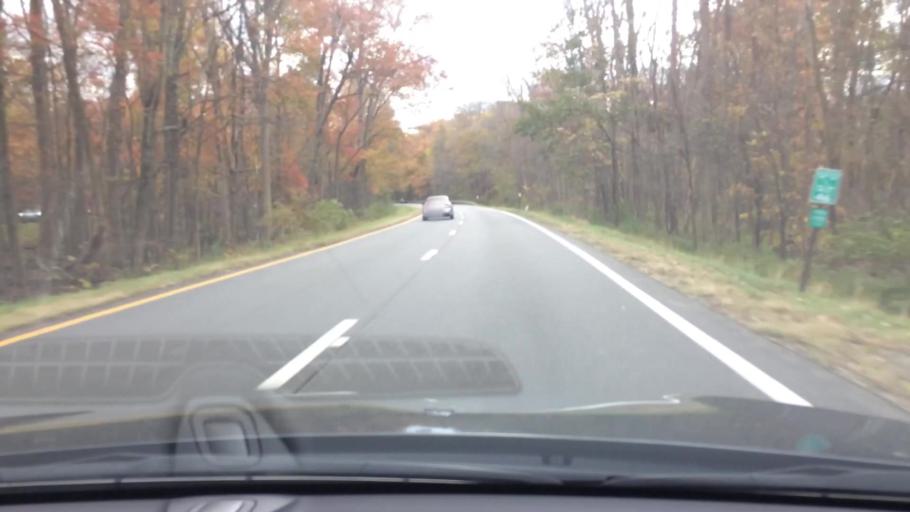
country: US
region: New York
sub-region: Dutchess County
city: Hillside Lake
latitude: 41.6516
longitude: -73.7909
